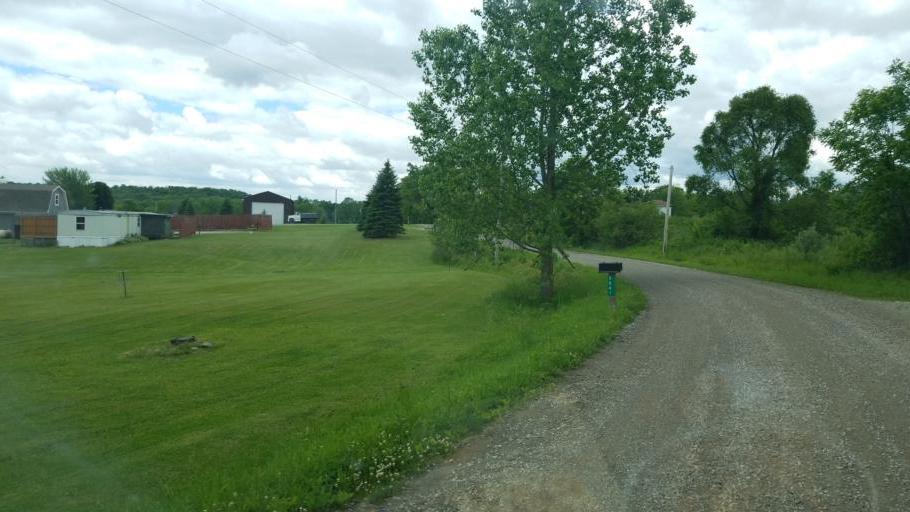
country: US
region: Ohio
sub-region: Richland County
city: Lexington
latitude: 40.6457
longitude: -82.6774
